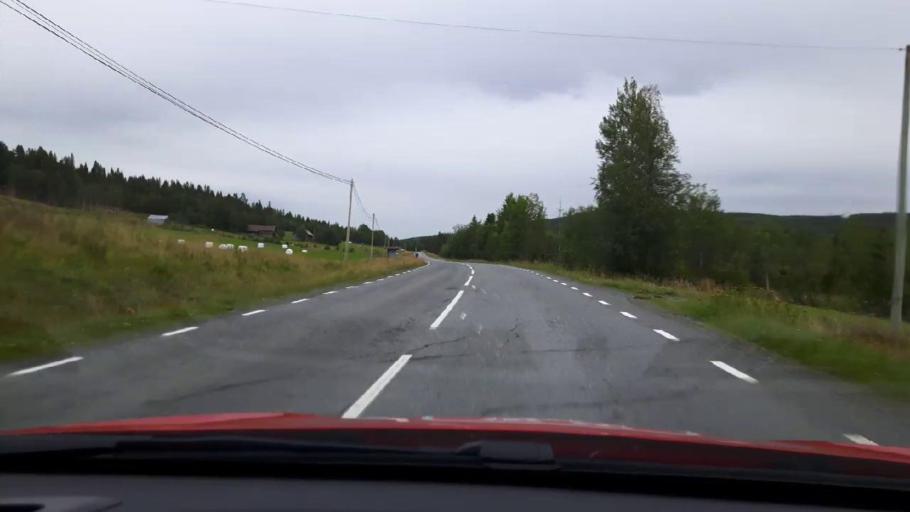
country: SE
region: Jaemtland
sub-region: Are Kommun
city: Jarpen
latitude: 63.3999
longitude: 13.3729
